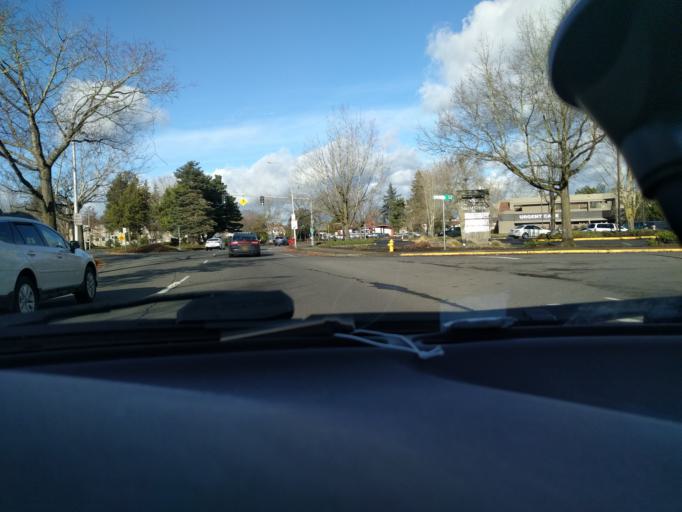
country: US
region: Oregon
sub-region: Marion County
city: Salem
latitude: 44.9548
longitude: -123.0208
